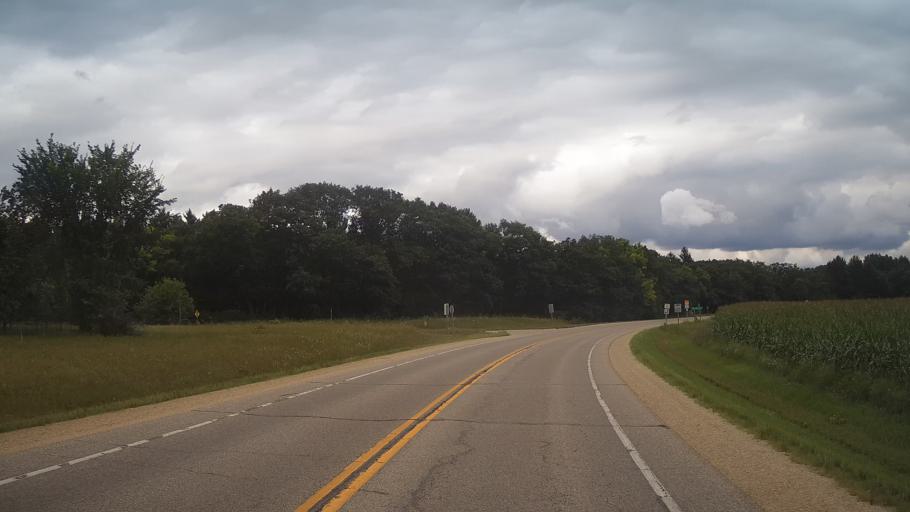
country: US
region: Wisconsin
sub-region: Waushara County
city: Wautoma
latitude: 44.0661
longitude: -89.3648
